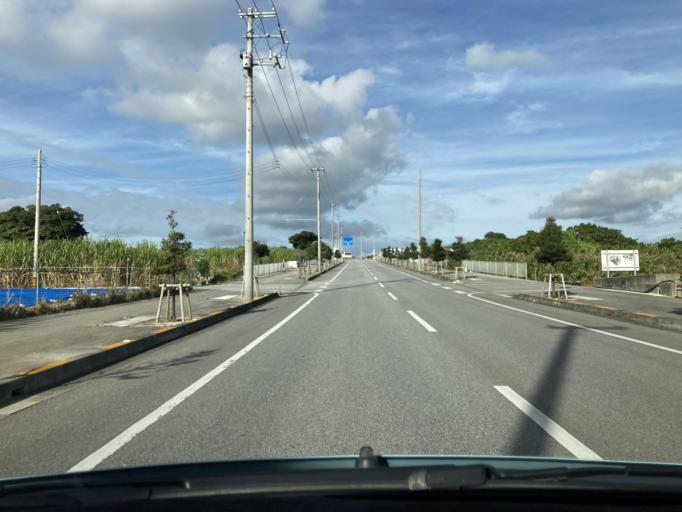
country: JP
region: Okinawa
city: Itoman
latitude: 26.1274
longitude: 127.6825
